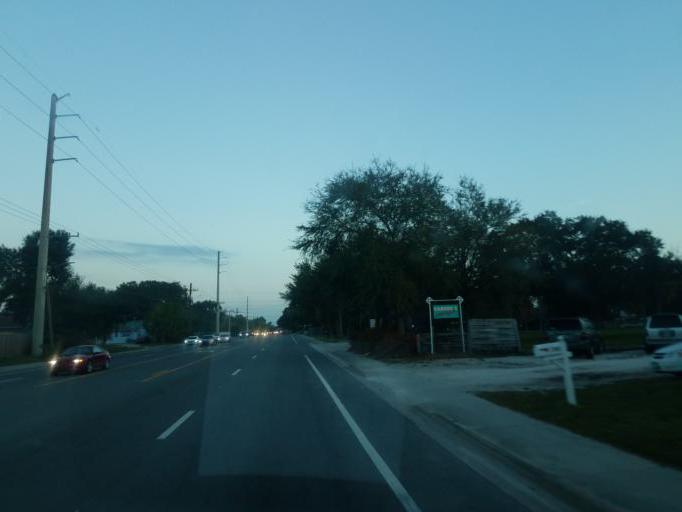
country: US
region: Florida
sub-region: Sarasota County
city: Kensington Park
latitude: 27.3530
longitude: -82.5056
